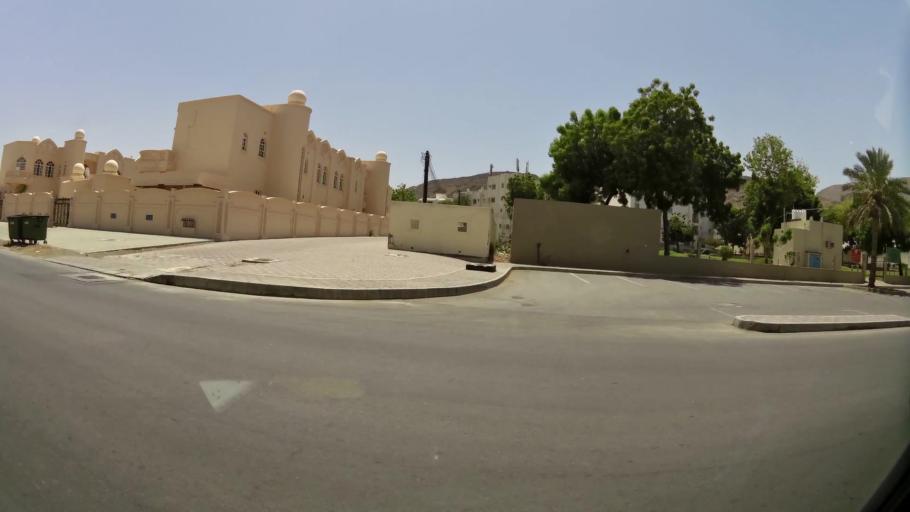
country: OM
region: Muhafazat Masqat
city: Bawshar
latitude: 23.5874
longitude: 58.4523
